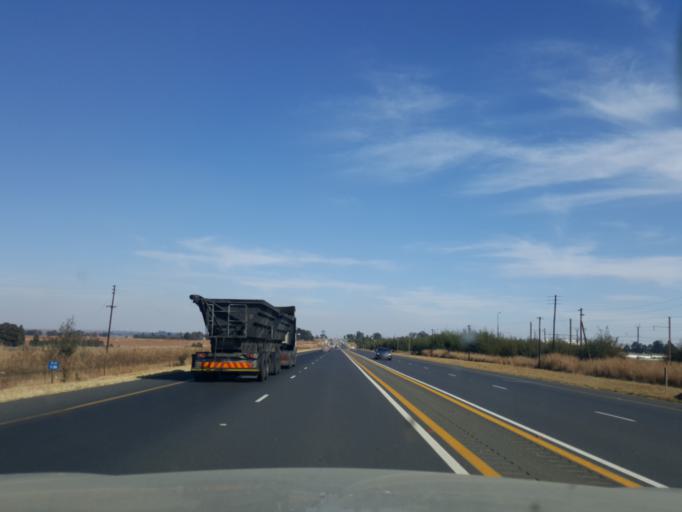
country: ZA
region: Mpumalanga
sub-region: Nkangala District Municipality
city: Belfast
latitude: -25.7978
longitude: 29.9104
